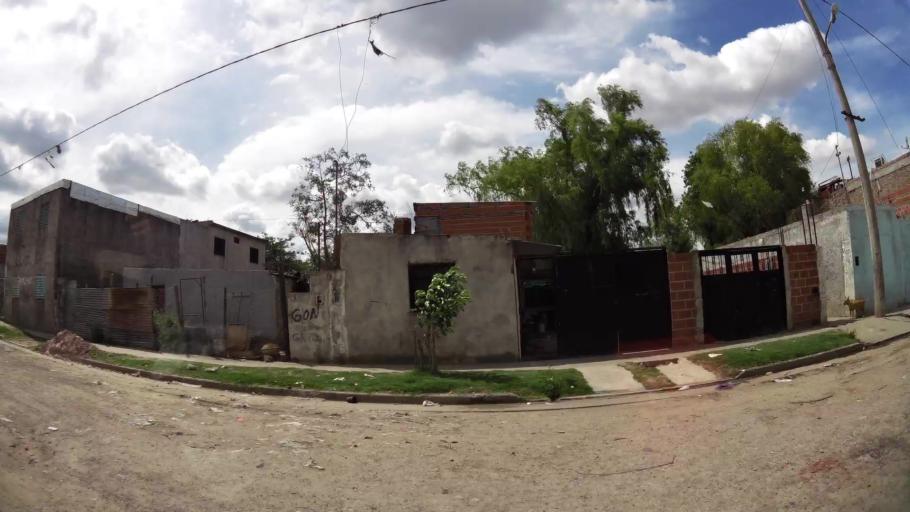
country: AR
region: Santa Fe
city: Gobernador Galvez
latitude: -33.0158
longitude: -60.6425
